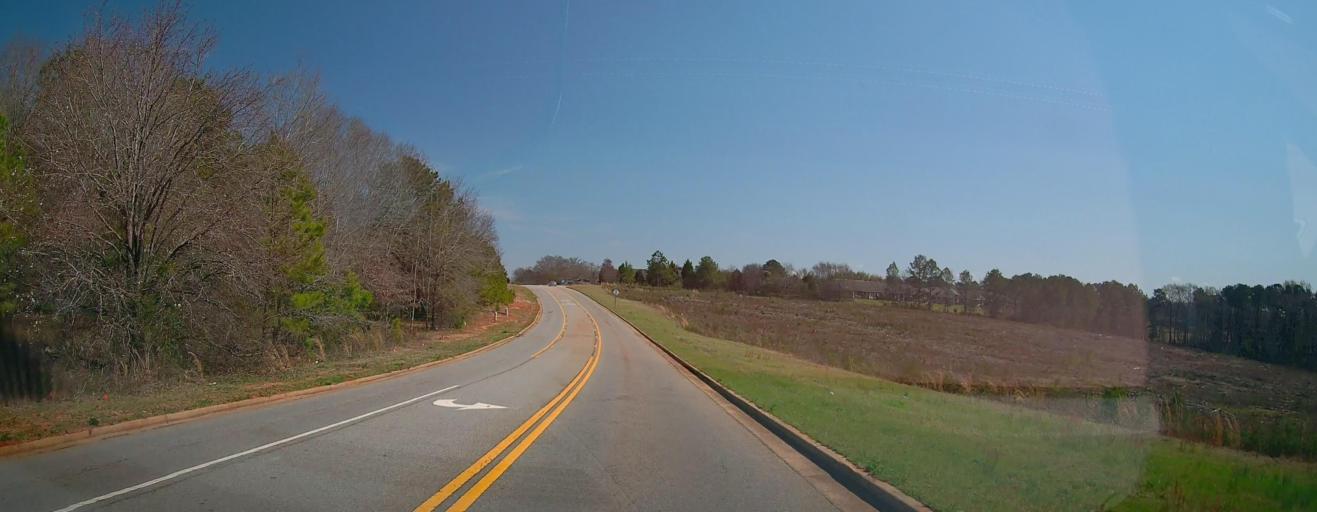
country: US
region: Georgia
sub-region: Houston County
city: Centerville
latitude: 32.6122
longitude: -83.7021
